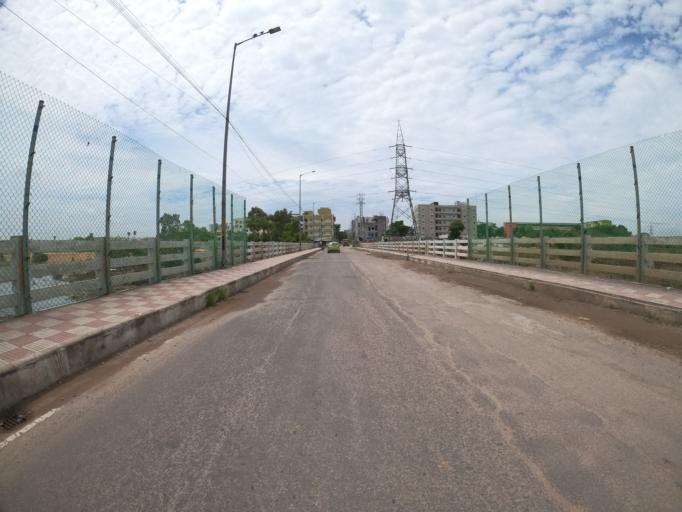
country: IN
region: Telangana
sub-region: Hyderabad
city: Hyderabad
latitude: 17.3713
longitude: 78.4121
